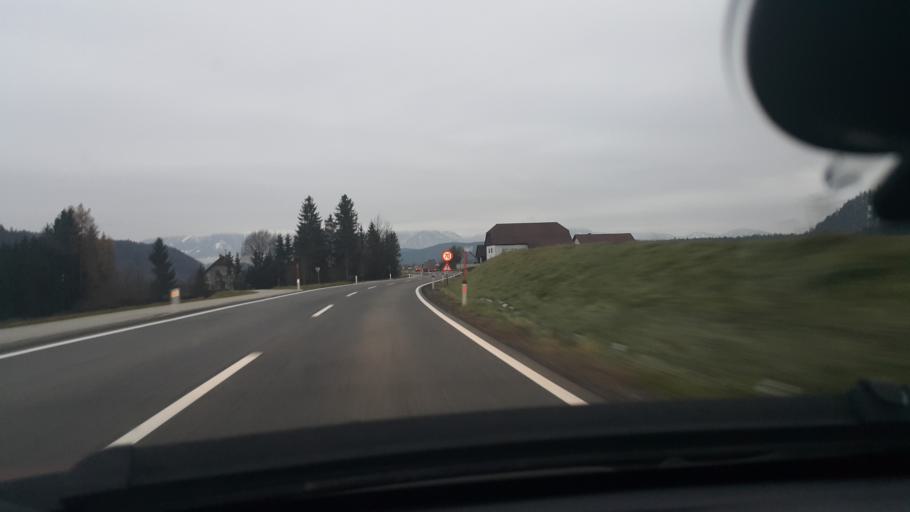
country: AT
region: Carinthia
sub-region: Politischer Bezirk Volkermarkt
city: Ruden
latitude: 46.6675
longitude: 14.7708
